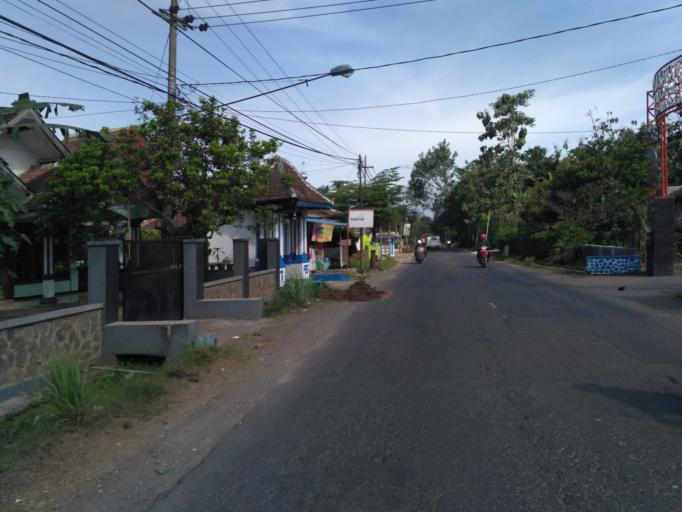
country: ID
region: East Java
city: Golek
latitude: -8.0698
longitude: 112.6265
